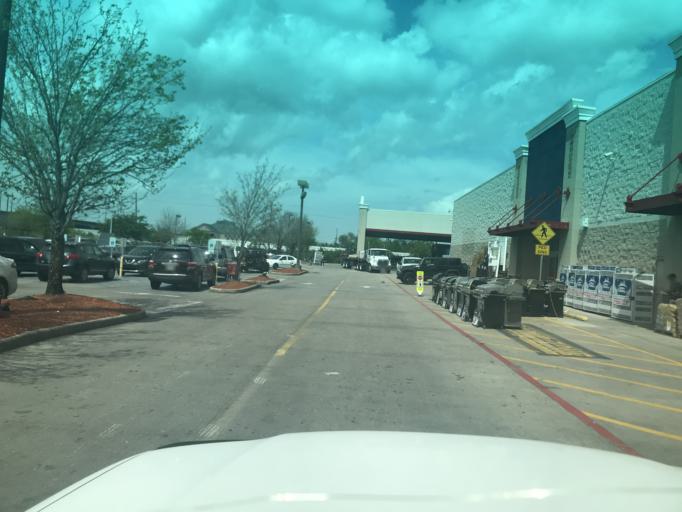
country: US
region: Louisiana
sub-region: Orleans Parish
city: New Orleans
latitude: 29.9838
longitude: -90.0568
